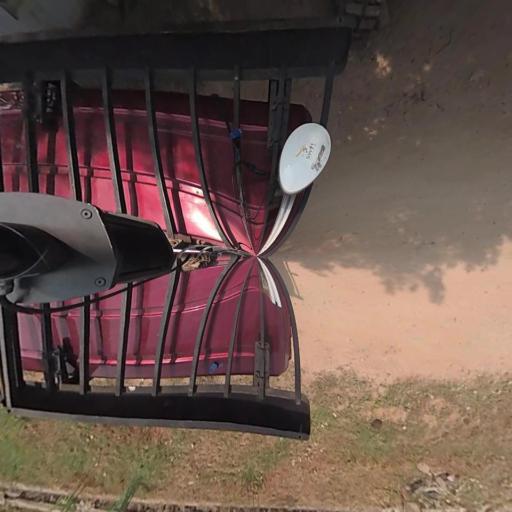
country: IN
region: Telangana
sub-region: Nalgonda
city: Nalgonda
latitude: 17.2133
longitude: 79.1575
